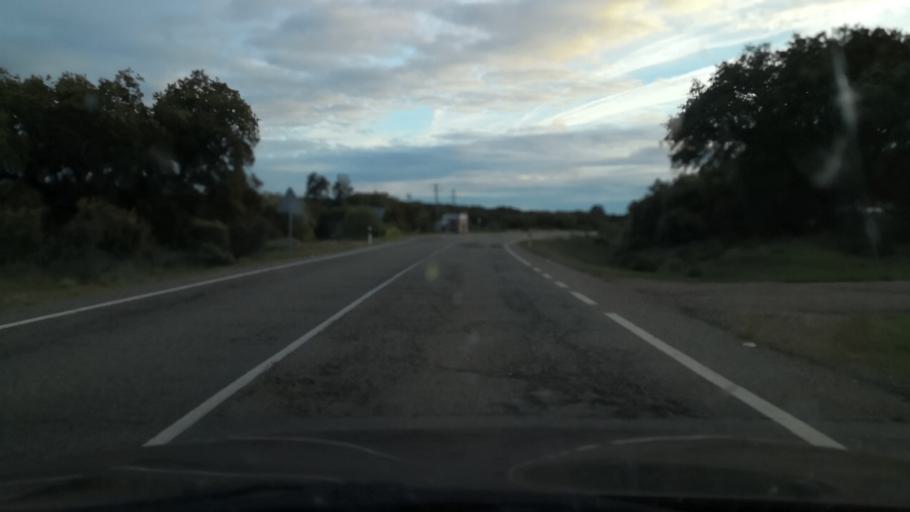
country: ES
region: Extremadura
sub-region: Provincia de Badajoz
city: La Roca de la Sierra
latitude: 39.1388
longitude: -6.6564
